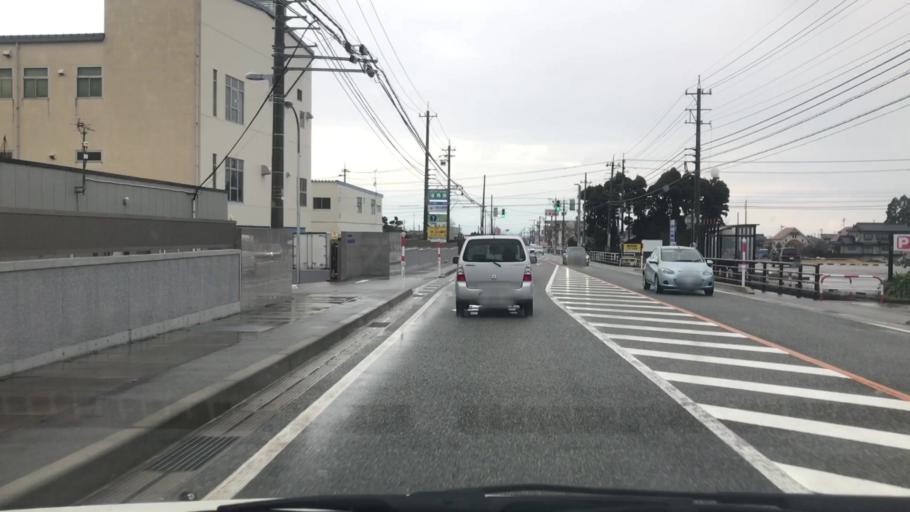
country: JP
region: Toyama
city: Yatsuomachi-higashikumisaka
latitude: 36.6094
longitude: 137.2045
